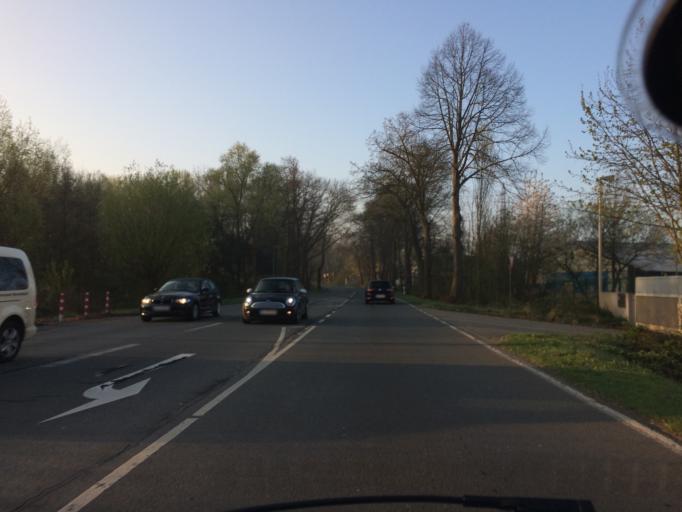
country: DE
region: North Rhine-Westphalia
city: Hattingen
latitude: 51.4222
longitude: 7.1680
